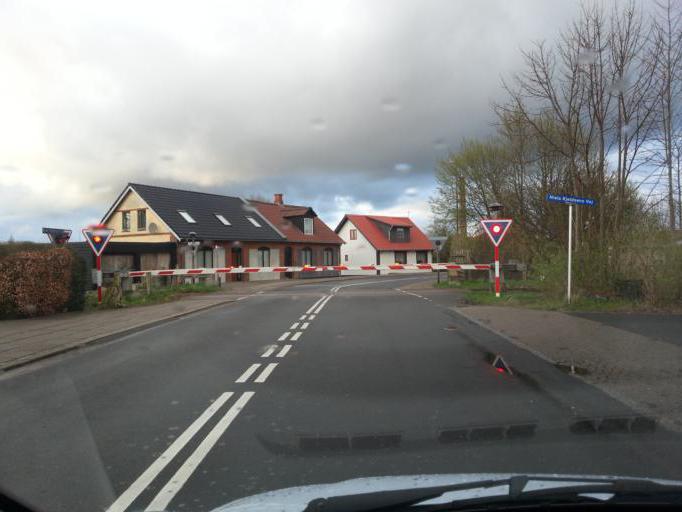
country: DK
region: Central Jutland
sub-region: Holstebro Kommune
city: Holstebro
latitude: 56.3535
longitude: 8.6108
